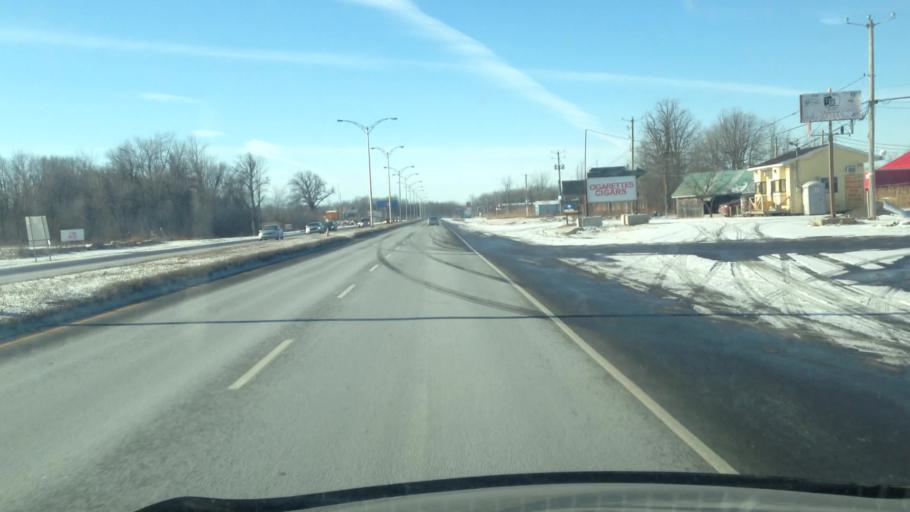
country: CA
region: Quebec
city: Montreal-Ouest
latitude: 45.4017
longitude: -73.6758
